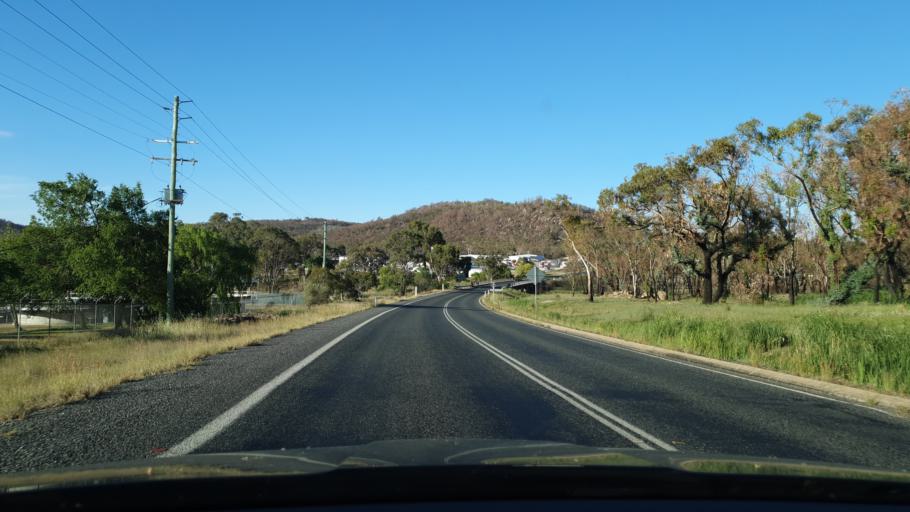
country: AU
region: Queensland
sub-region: Southern Downs
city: Stanthorpe
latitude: -28.6553
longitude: 151.9175
